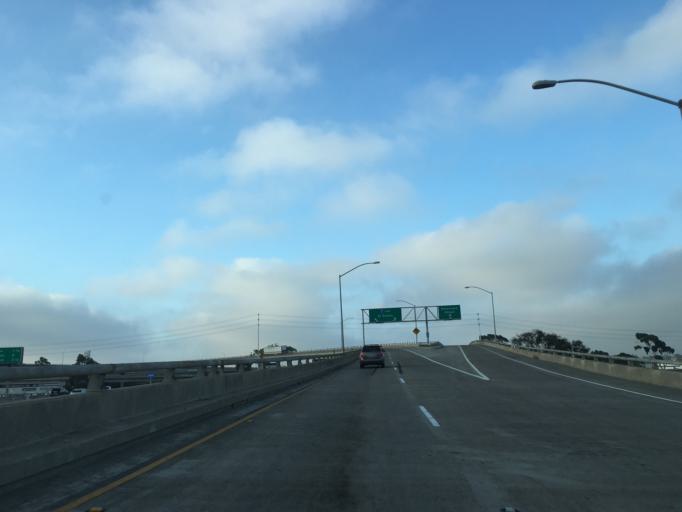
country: US
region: California
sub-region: San Diego County
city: San Diego
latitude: 32.7622
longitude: -117.2051
